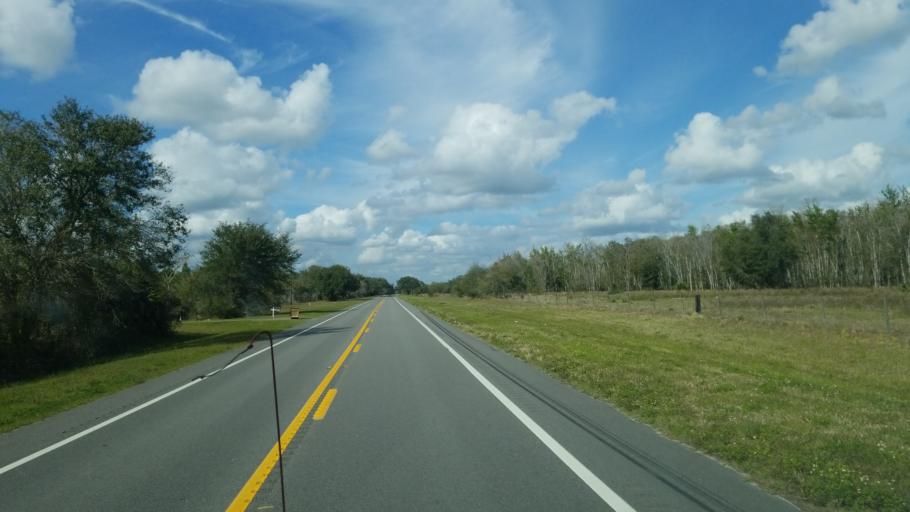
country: US
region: Florida
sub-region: Brevard County
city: June Park
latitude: 27.9457
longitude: -80.9974
